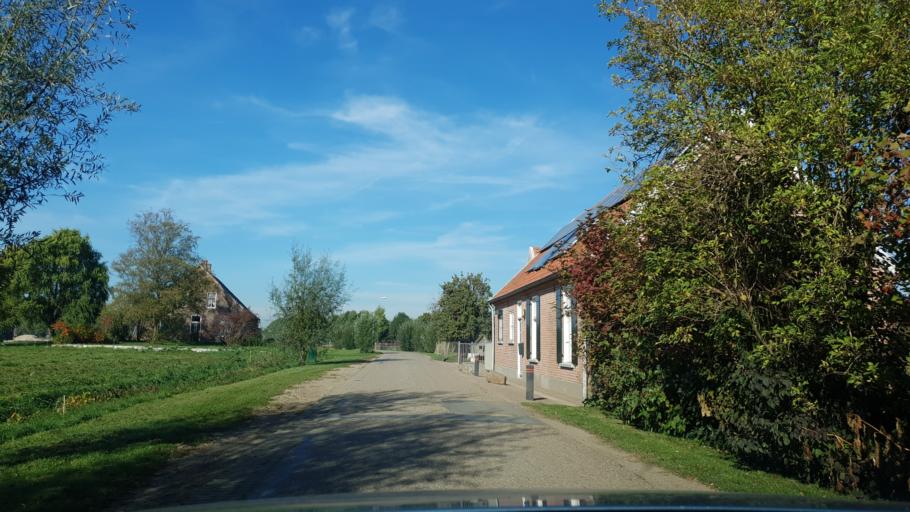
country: NL
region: Gelderland
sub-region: Gemeente Wijchen
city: Bergharen
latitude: 51.8708
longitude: 5.7035
